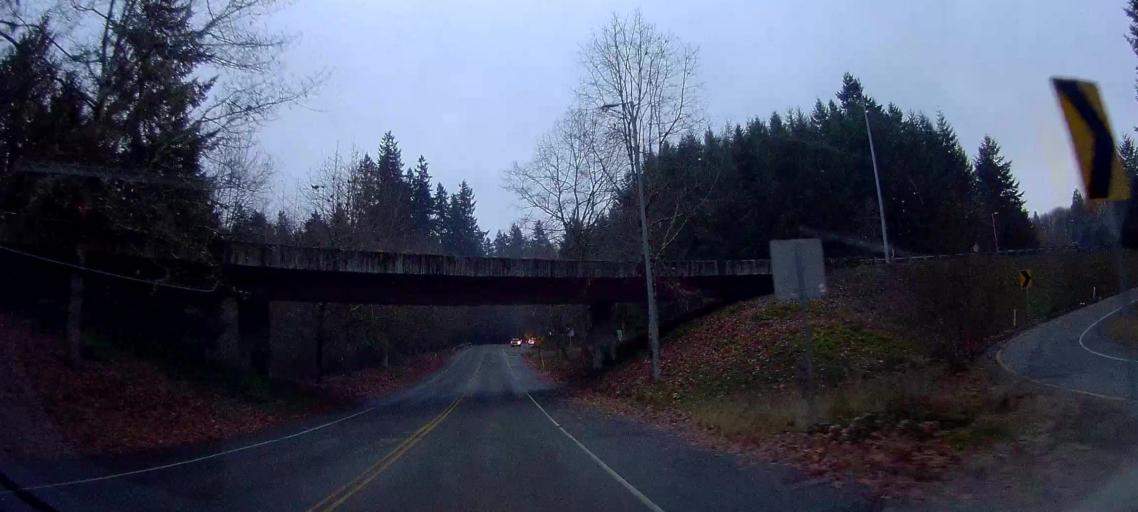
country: US
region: Washington
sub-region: Thurston County
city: Olympia
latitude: 47.0319
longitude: -122.8902
